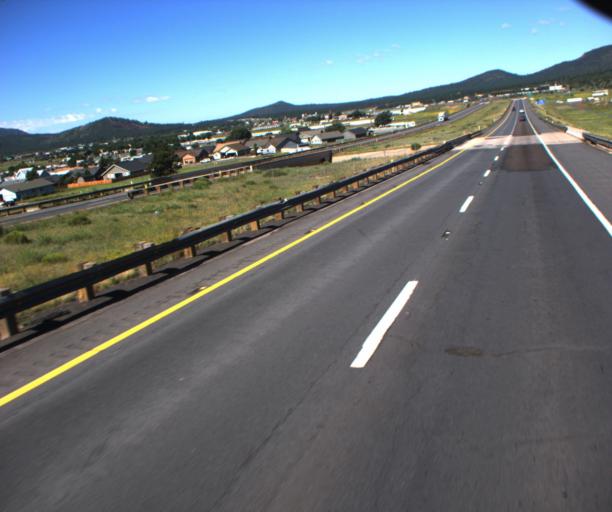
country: US
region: Arizona
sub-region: Coconino County
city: Williams
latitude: 35.2642
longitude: -112.1721
